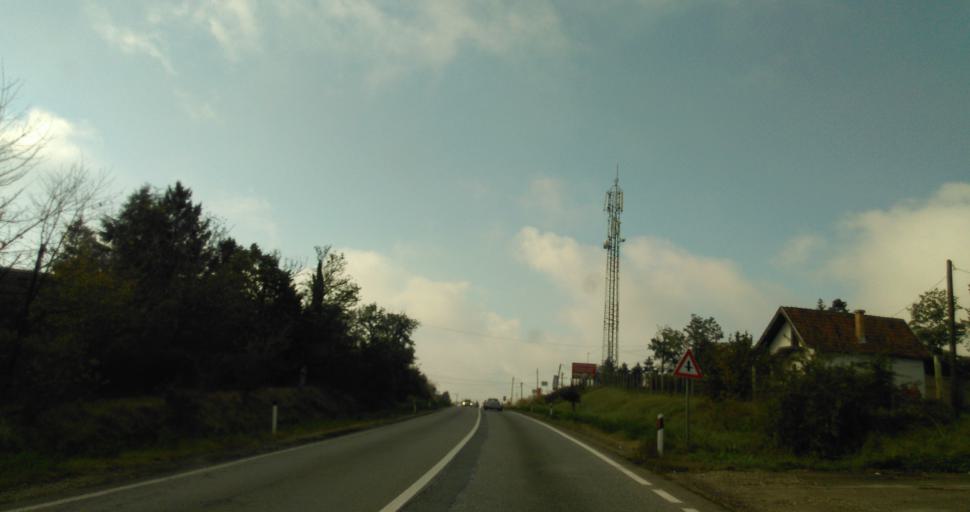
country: RS
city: Vranic
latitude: 44.6127
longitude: 20.3609
